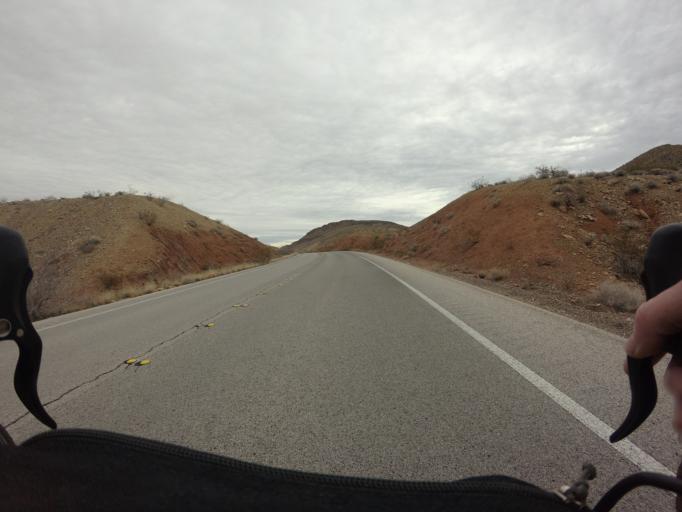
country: US
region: Nevada
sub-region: Clark County
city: Boulder City
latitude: 36.2272
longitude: -114.5830
